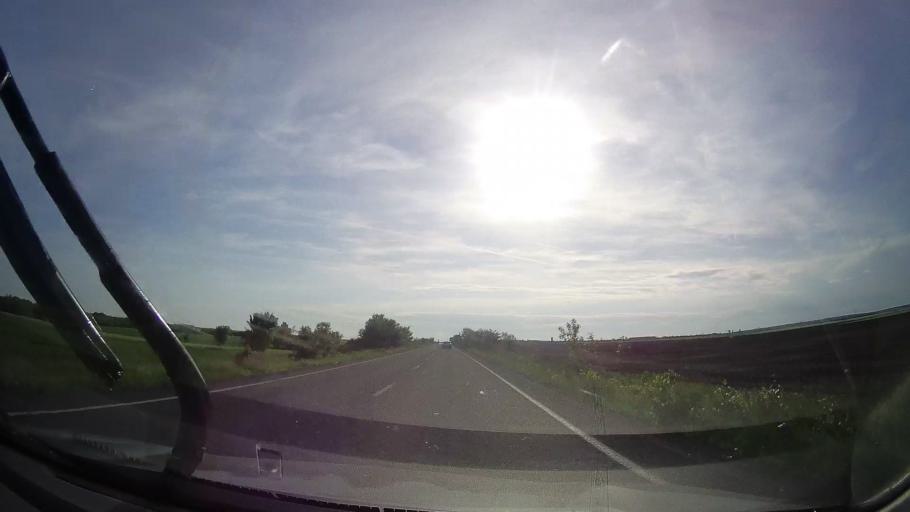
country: RO
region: Timis
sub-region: Comuna Topolovatu Mare
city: Topolovatu Mare
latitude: 45.7758
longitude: 21.6506
